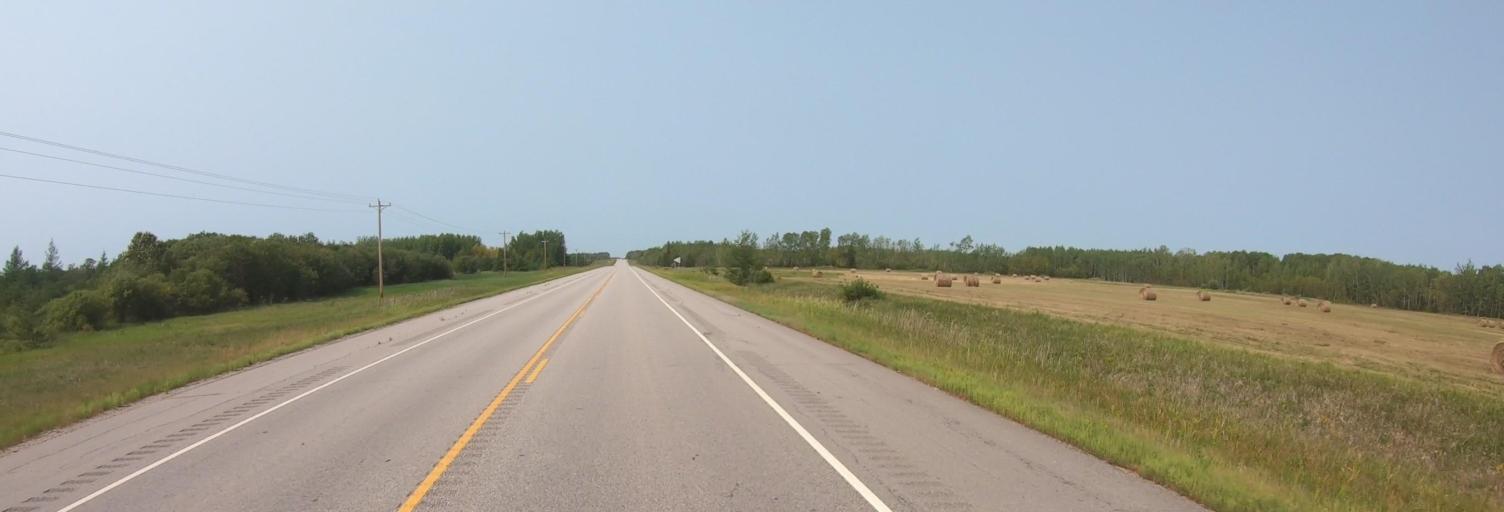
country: CA
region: Ontario
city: Fort Frances
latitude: 48.4100
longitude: -93.1428
